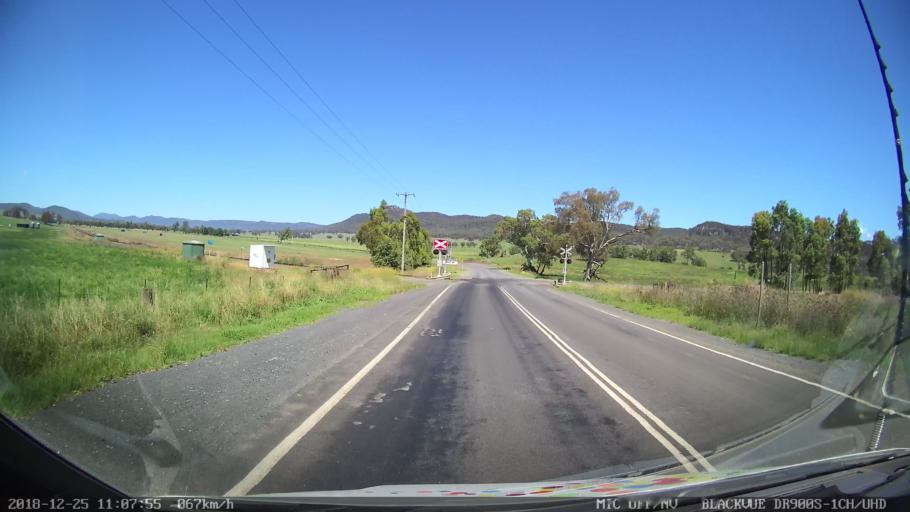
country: AU
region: New South Wales
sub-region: Upper Hunter Shire
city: Merriwa
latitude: -32.3998
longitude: 150.1295
